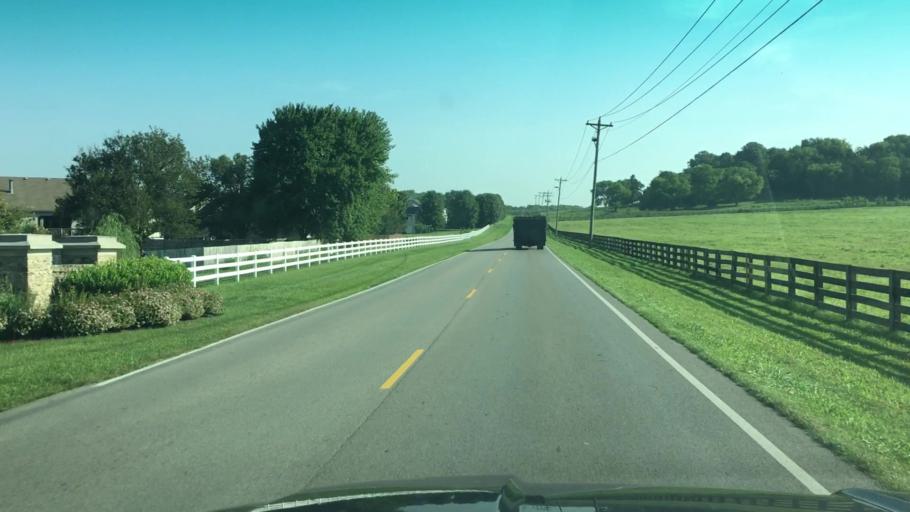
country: US
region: Tennessee
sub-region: Williamson County
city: Thompson's Station
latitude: 35.7852
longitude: -86.8784
